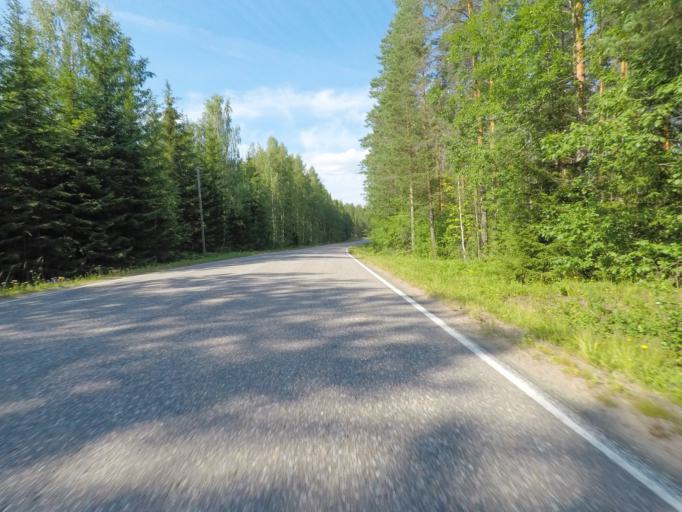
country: FI
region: Southern Savonia
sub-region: Mikkeli
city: Puumala
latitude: 61.6127
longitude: 28.2198
